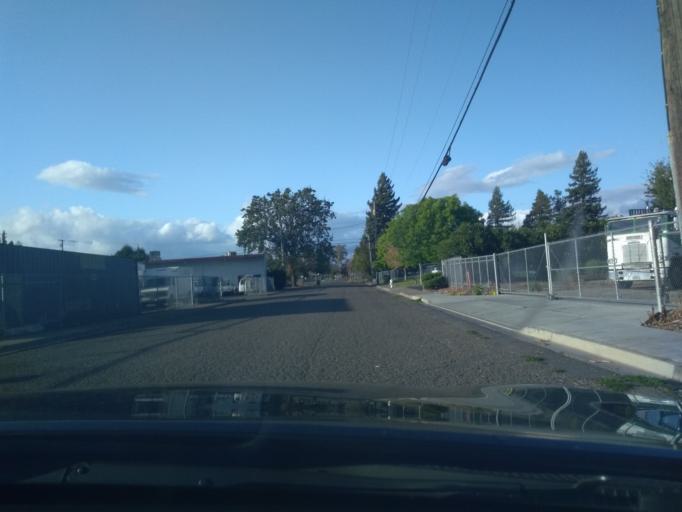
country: US
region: California
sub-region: Mendocino County
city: Ukiah
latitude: 39.1607
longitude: -123.2073
